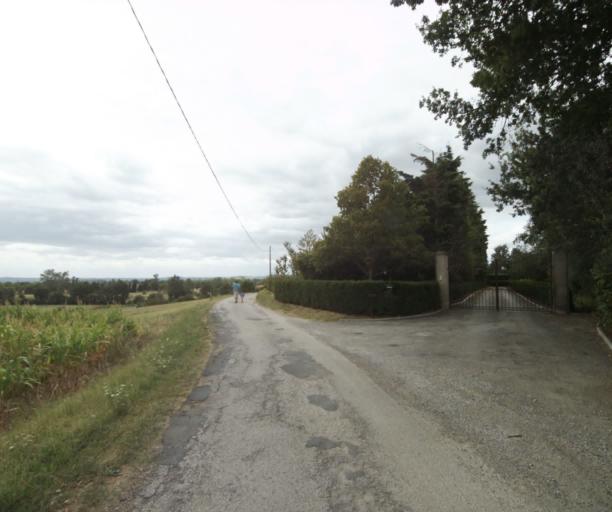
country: FR
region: Midi-Pyrenees
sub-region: Departement du Tarn
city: Soreze
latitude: 43.4612
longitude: 2.0666
